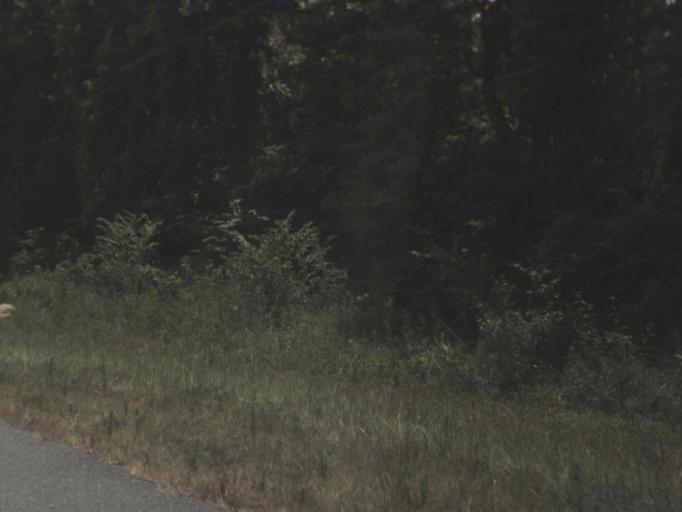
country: US
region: Florida
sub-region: Taylor County
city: Perry
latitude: 30.1411
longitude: -83.8816
